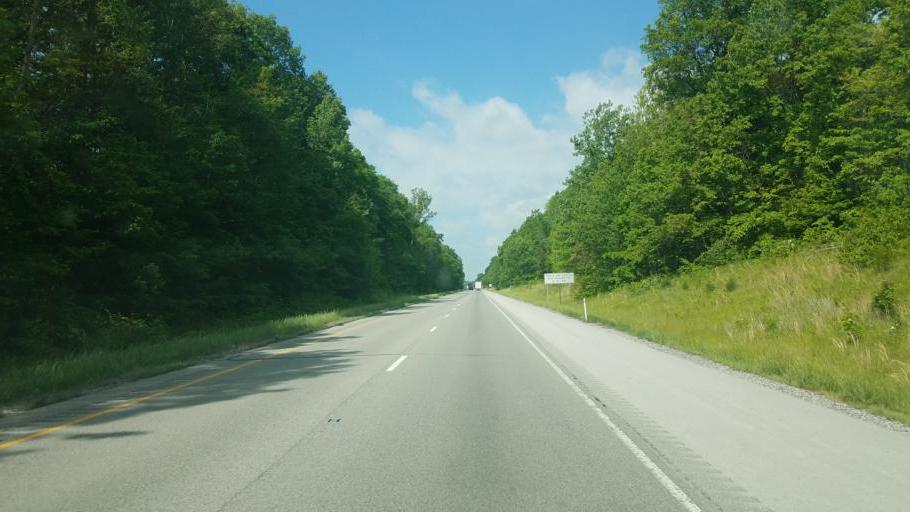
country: US
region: Indiana
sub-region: Putnam County
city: Cloverdale
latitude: 39.5215
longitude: -86.8977
